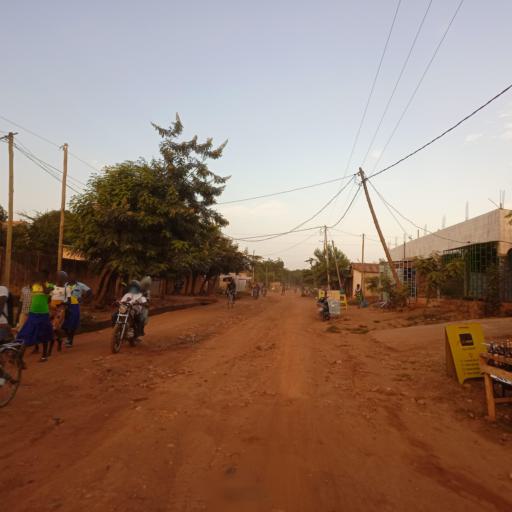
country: TG
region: Savanes
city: Dapaong
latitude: 10.8621
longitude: 0.1871
